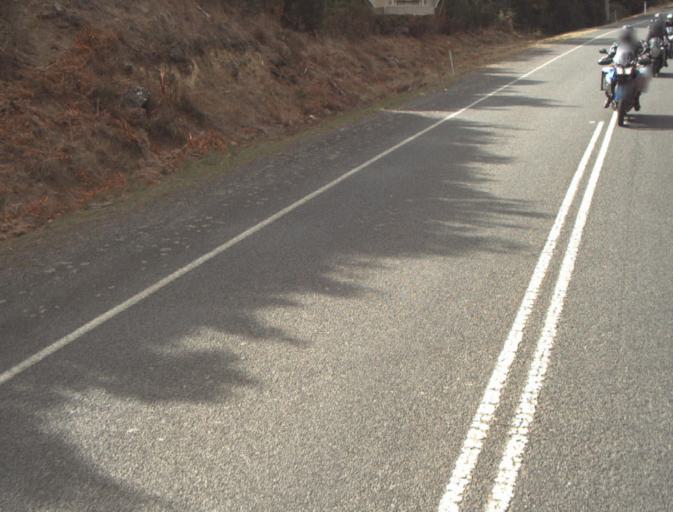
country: AU
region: Tasmania
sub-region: Launceston
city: Mayfield
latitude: -41.2758
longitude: 147.2191
